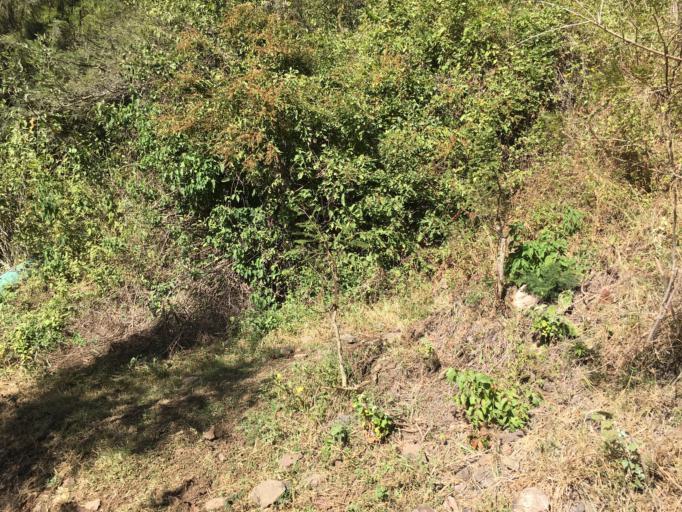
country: MX
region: Michoacan
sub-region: Morelia
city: Montana Monarca (Punta Altozano)
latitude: 19.6779
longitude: -101.1537
